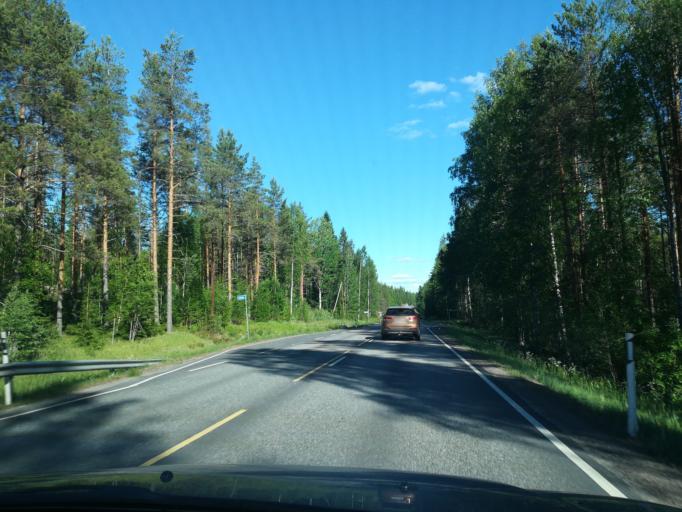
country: FI
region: South Karelia
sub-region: Imatra
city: Ruokolahti
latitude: 61.3655
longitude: 28.6873
